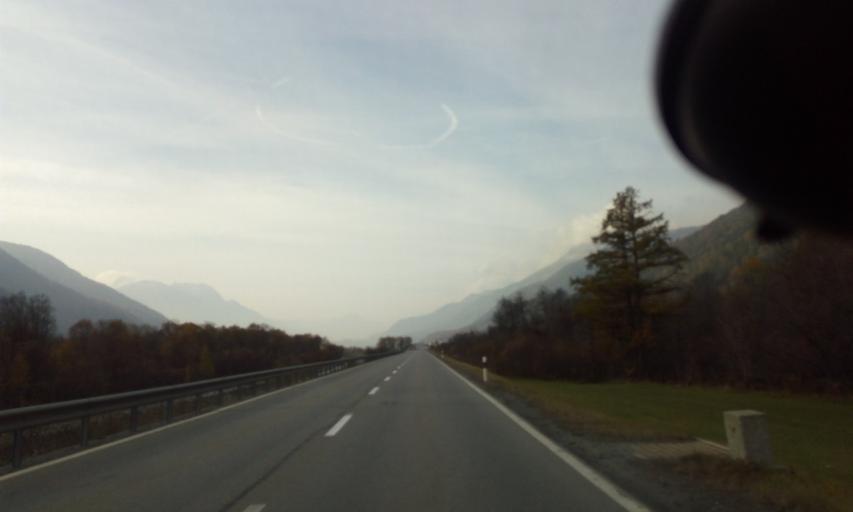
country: CH
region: Grisons
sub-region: Maloja District
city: Ponte
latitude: 46.5681
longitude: 9.9126
